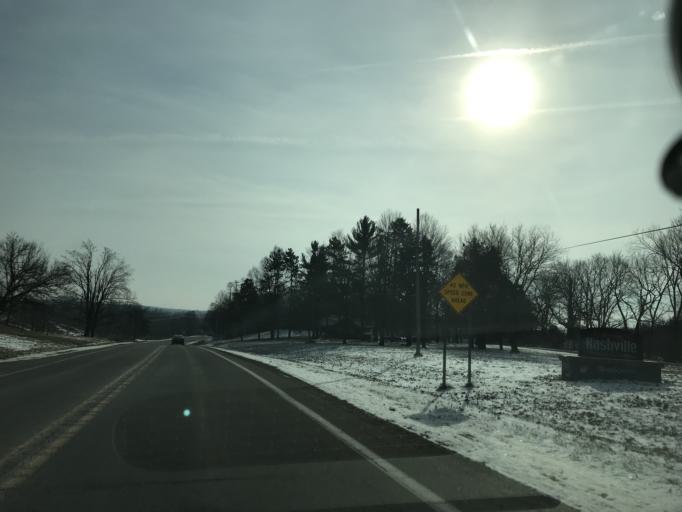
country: US
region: Michigan
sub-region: Barry County
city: Nashville
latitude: 42.6139
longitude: -85.0946
